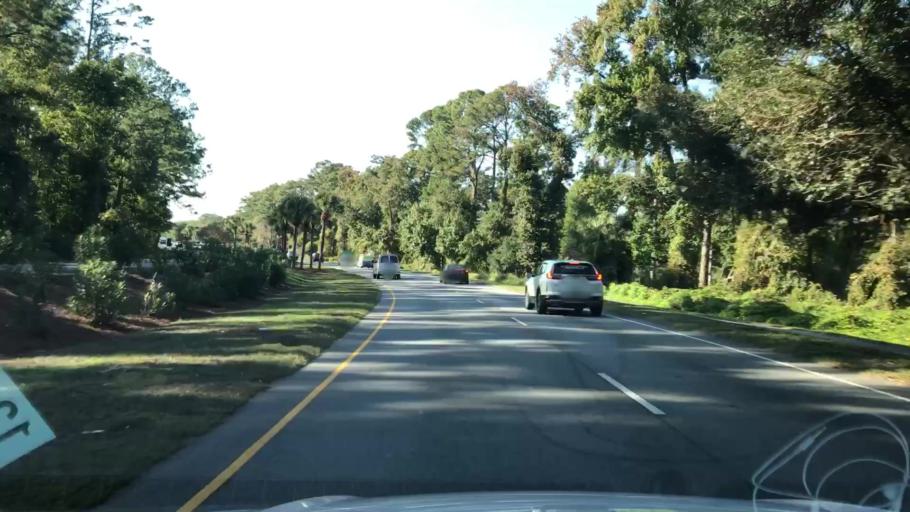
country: US
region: South Carolina
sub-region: Beaufort County
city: Hilton Head Island
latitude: 32.2141
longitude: -80.6971
